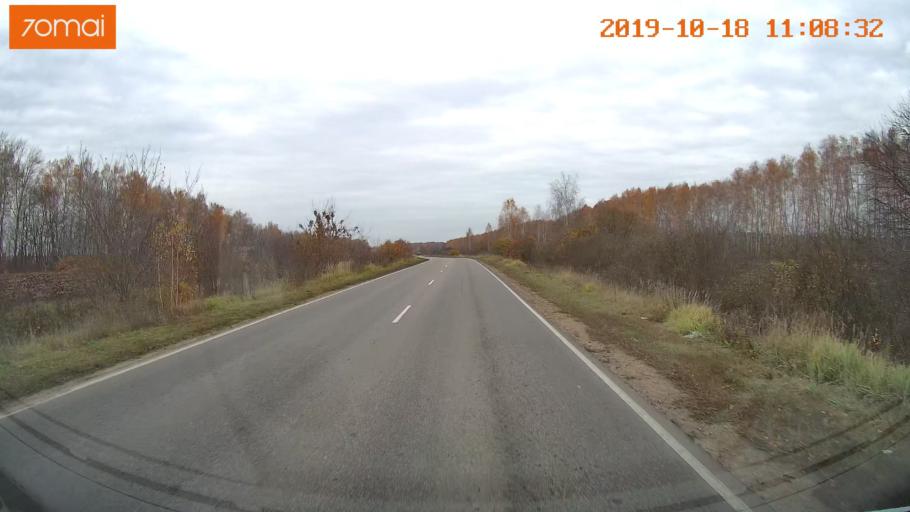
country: RU
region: Tula
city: Kimovsk
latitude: 53.9396
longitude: 38.5368
